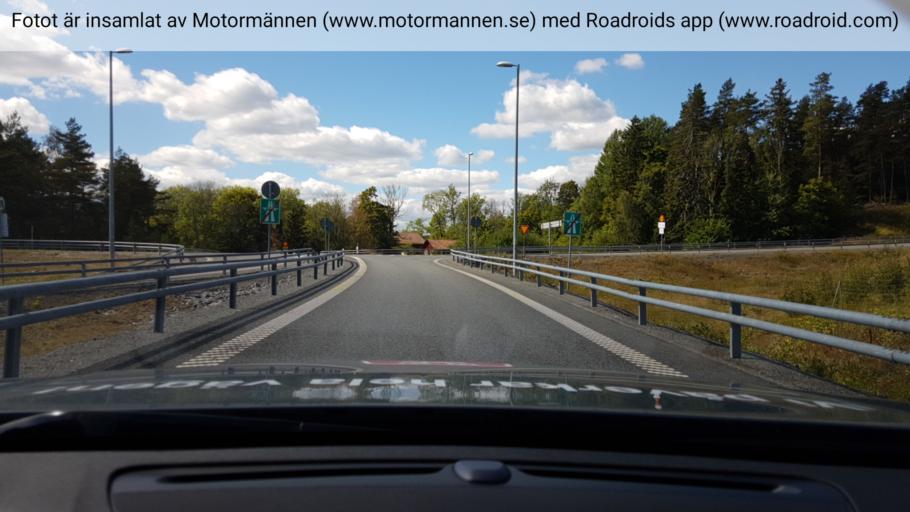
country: SE
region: Stockholm
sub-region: Haninge Kommun
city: Jordbro
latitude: 59.0695
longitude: 18.0640
